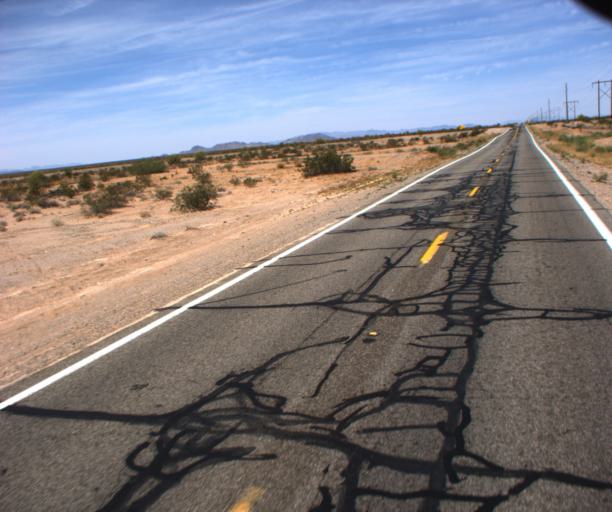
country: US
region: Arizona
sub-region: La Paz County
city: Quartzsite
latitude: 33.8218
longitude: -114.2170
